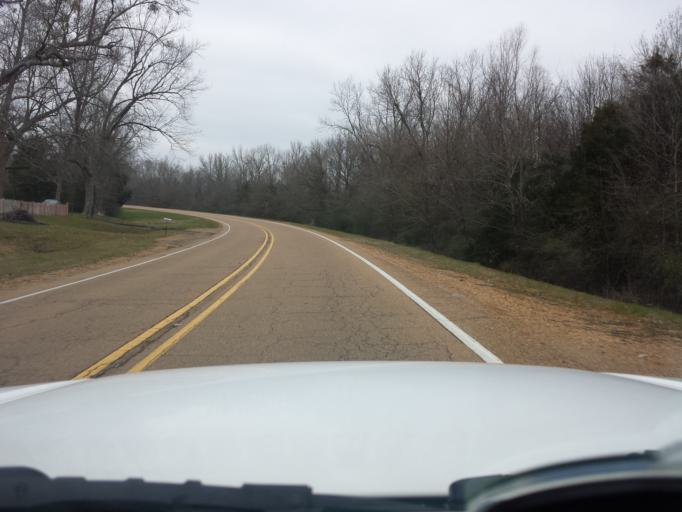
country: US
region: Mississippi
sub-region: Madison County
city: Canton
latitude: 32.7523
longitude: -90.1451
